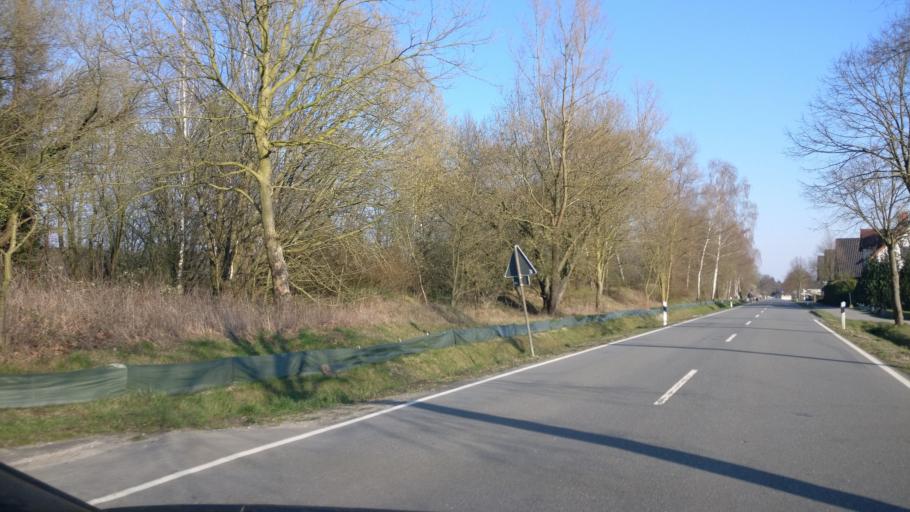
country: DE
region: North Rhine-Westphalia
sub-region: Regierungsbezirk Detmold
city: Lage
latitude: 52.0012
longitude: 8.7685
